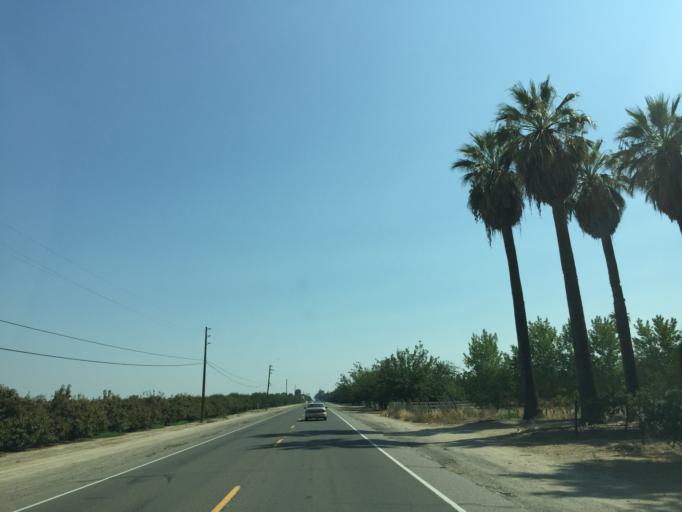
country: US
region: California
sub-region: Kings County
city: Lucerne
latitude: 36.3806
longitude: -119.6731
